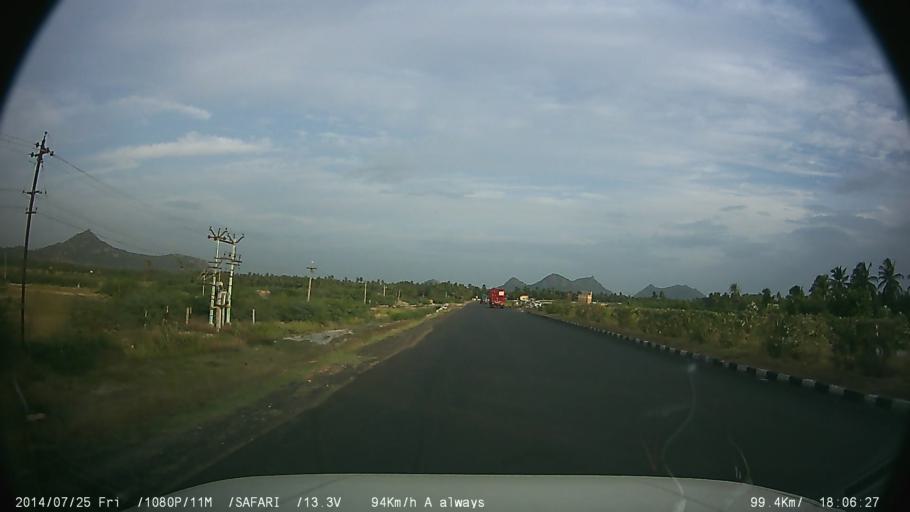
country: IN
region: Tamil Nadu
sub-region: Krishnagiri
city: Kaverippattanam
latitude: 12.4285
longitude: 78.2256
